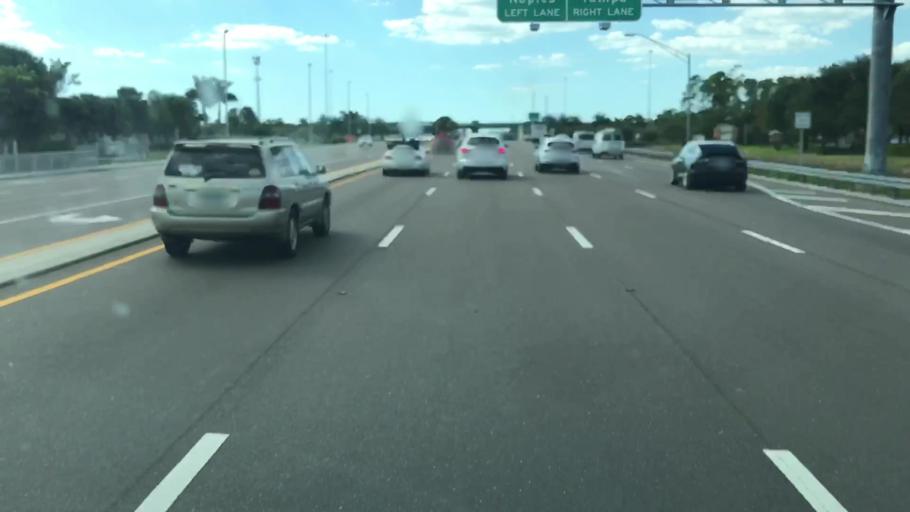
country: US
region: Florida
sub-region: Collier County
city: Vineyards
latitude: 26.2729
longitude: -81.7385
